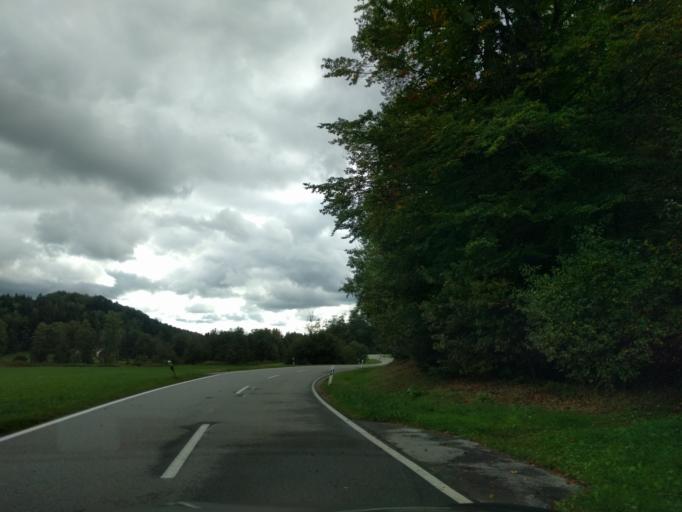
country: DE
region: Bavaria
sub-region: Lower Bavaria
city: Auerbach
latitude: 48.8300
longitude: 13.0917
